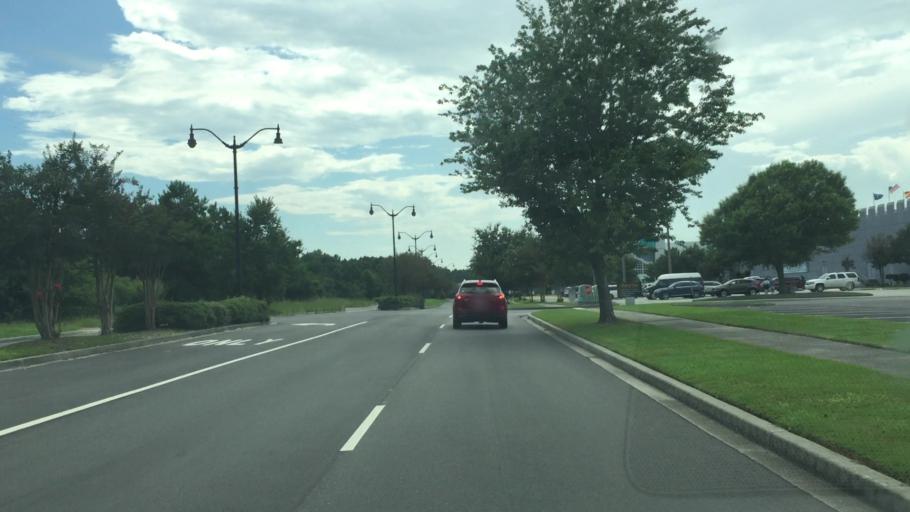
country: US
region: South Carolina
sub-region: Horry County
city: Forestbrook
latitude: 33.7115
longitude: -78.9311
